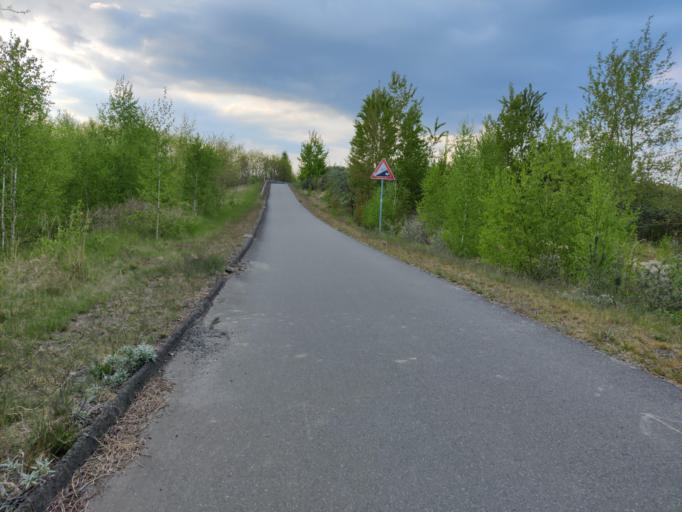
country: DE
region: Saxony
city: Rotha
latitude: 51.2368
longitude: 12.4414
